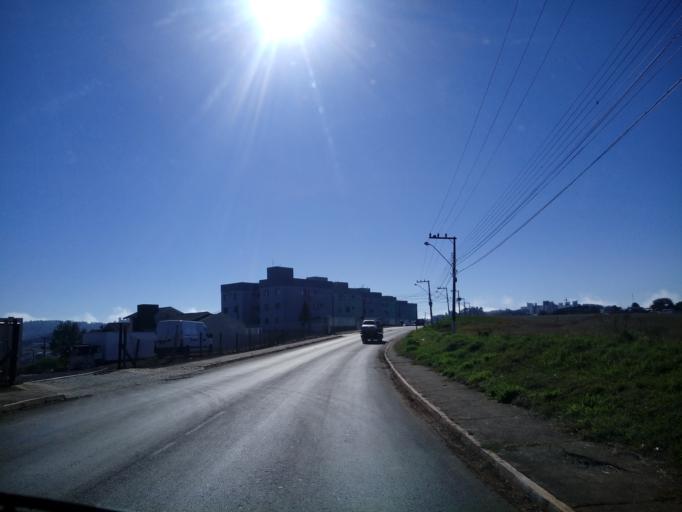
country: BR
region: Santa Catarina
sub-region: Chapeco
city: Chapeco
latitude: -27.0712
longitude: -52.6106
